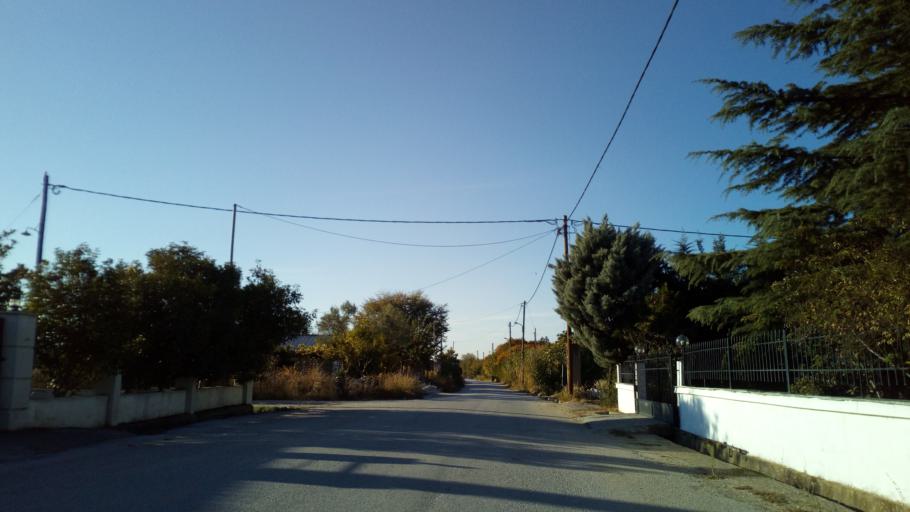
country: GR
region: Central Macedonia
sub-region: Nomos Thessalonikis
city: Gerakarou
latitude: 40.6386
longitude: 23.2433
